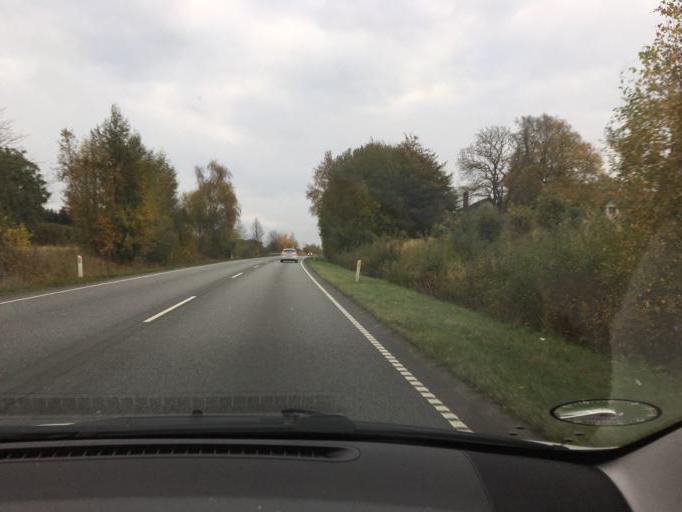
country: DK
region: South Denmark
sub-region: Fredericia Kommune
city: Fredericia
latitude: 55.6177
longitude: 9.7469
